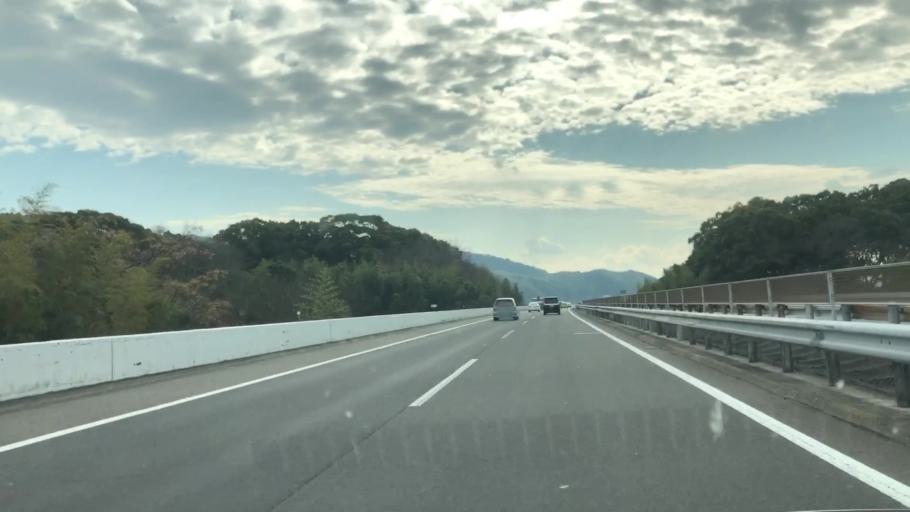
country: JP
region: Fukuoka
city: Setakamachi-takayanagi
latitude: 33.1828
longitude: 130.5184
